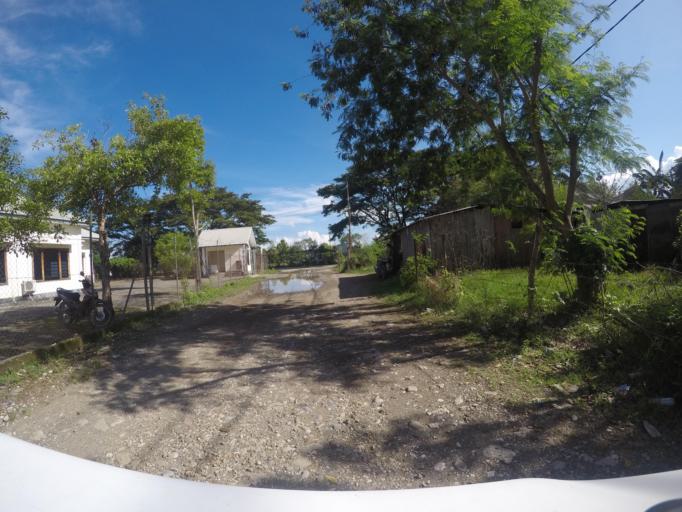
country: TL
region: Bobonaro
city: Maliana
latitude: -8.9929
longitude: 125.1910
